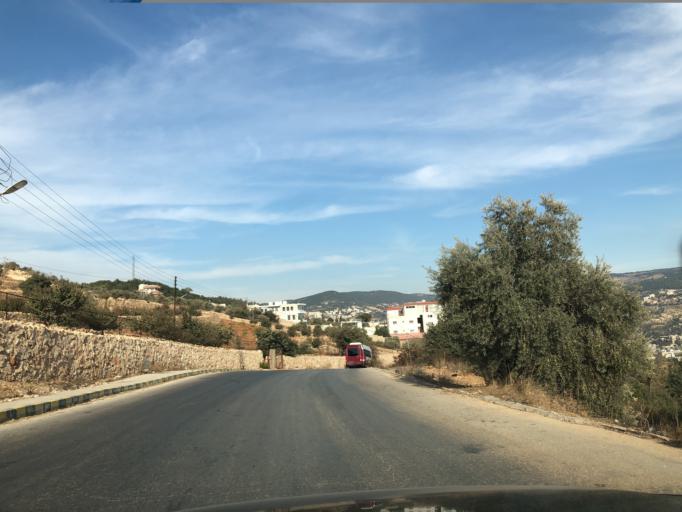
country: JO
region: Ajlun
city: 'Ajlun
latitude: 32.3291
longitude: 35.7320
